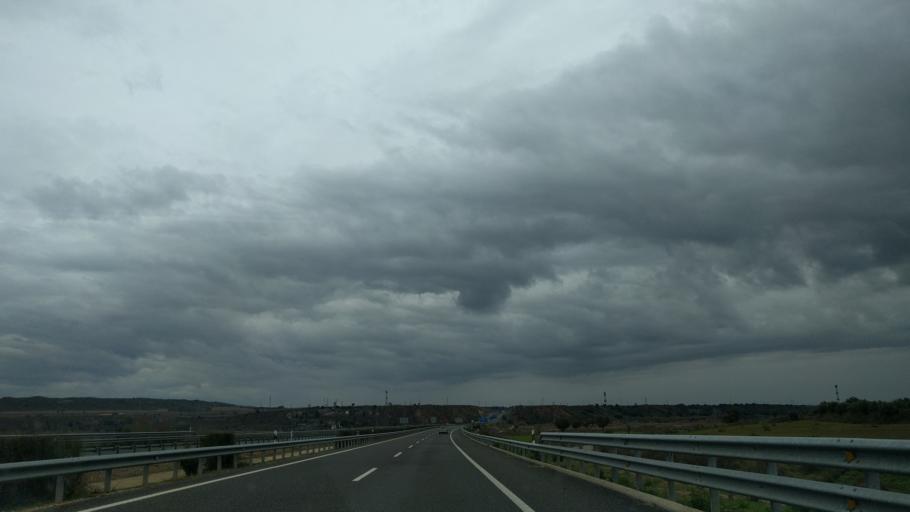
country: ES
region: Aragon
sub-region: Provincia de Huesca
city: Castejon del Puente
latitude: 41.9620
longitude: 0.1681
